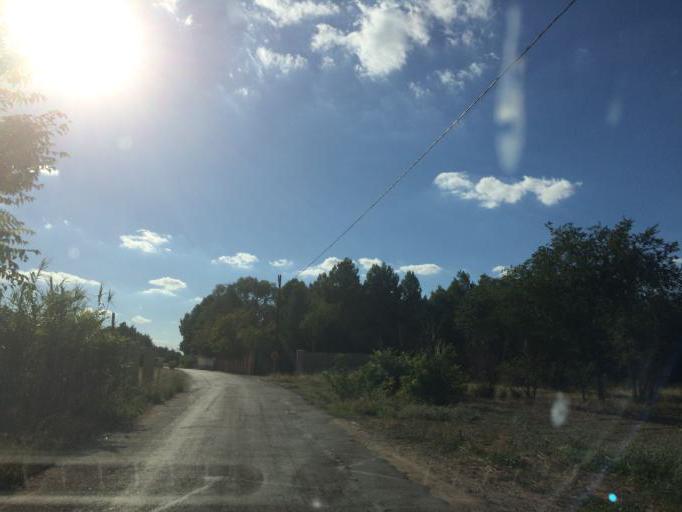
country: ES
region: Castille-La Mancha
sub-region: Provincia de Albacete
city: Albacete
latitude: 38.9939
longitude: -1.8803
